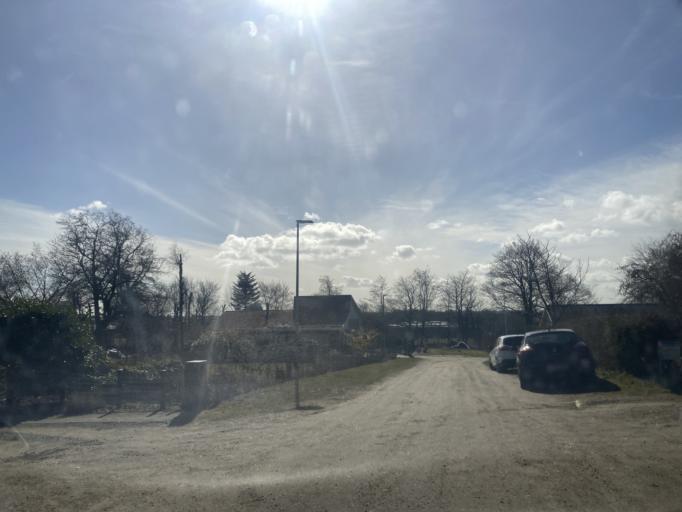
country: DK
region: Central Jutland
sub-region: Viborg Kommune
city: Viborg
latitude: 56.4600
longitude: 9.3578
